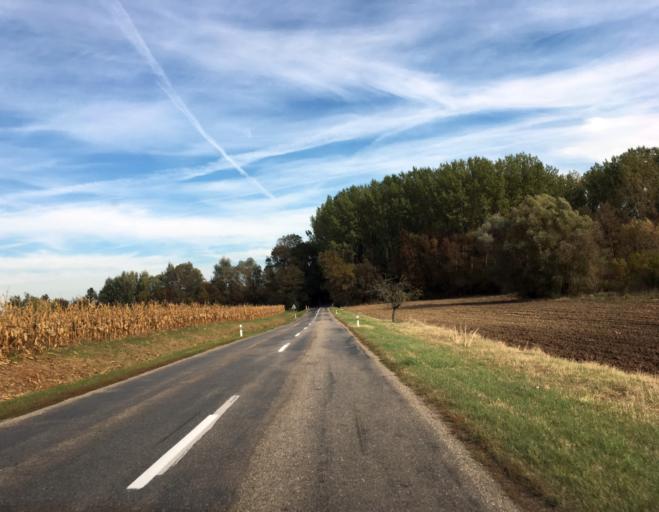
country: SK
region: Nitriansky
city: Svodin
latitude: 48.0032
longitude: 18.4127
